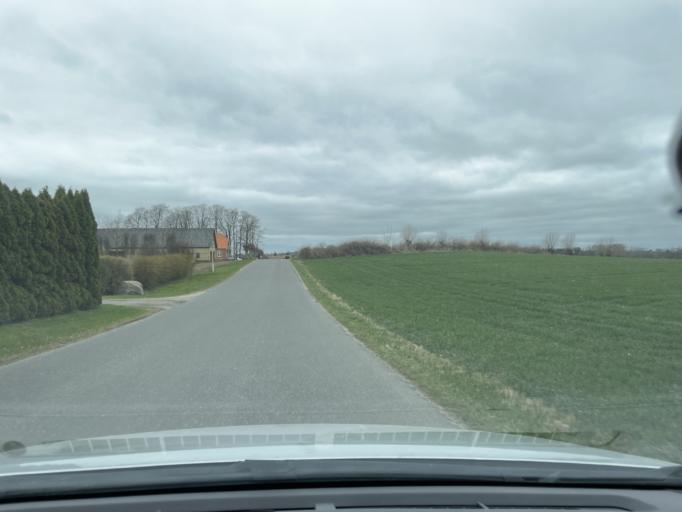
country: DK
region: South Denmark
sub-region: Nyborg Kommune
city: Nyborg
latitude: 55.3520
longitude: 10.7583
